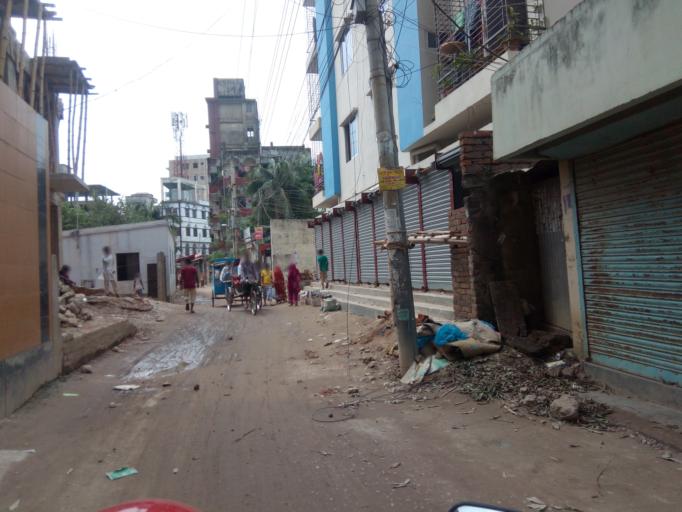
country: BD
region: Dhaka
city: Paltan
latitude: 23.7445
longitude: 90.4392
